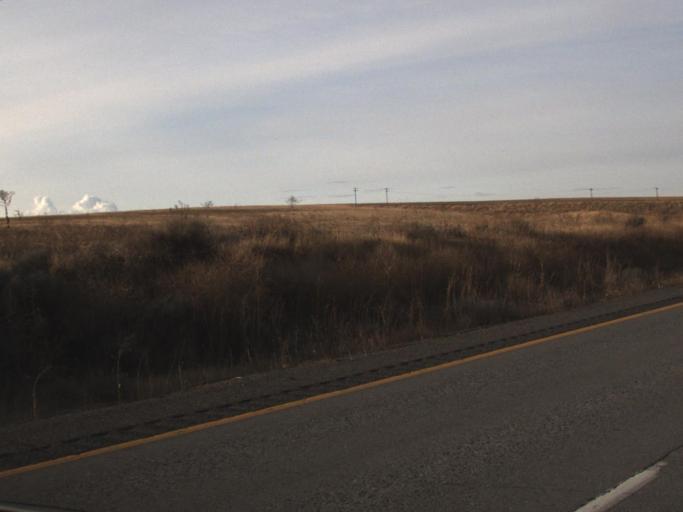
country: US
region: Washington
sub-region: Benton County
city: Highland
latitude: 46.0586
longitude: -119.2236
